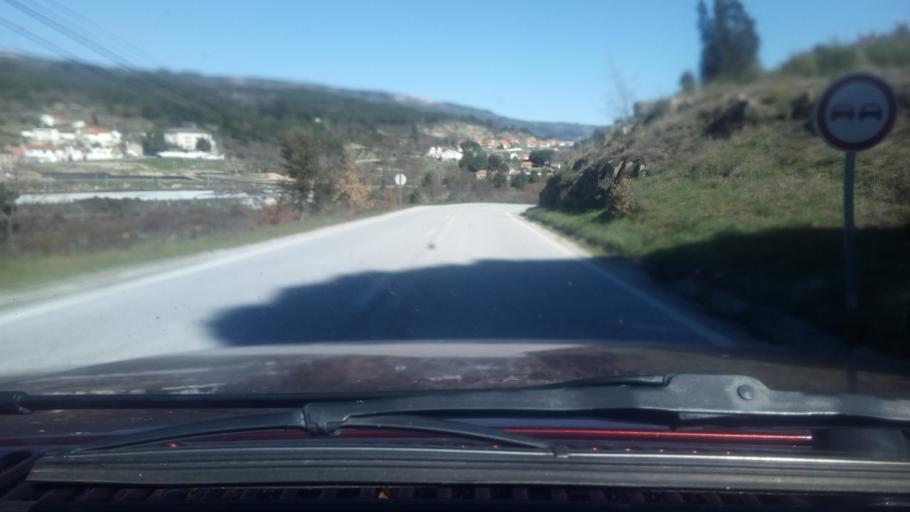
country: PT
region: Guarda
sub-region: Fornos de Algodres
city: Fornos de Algodres
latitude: 40.6081
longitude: -7.5241
